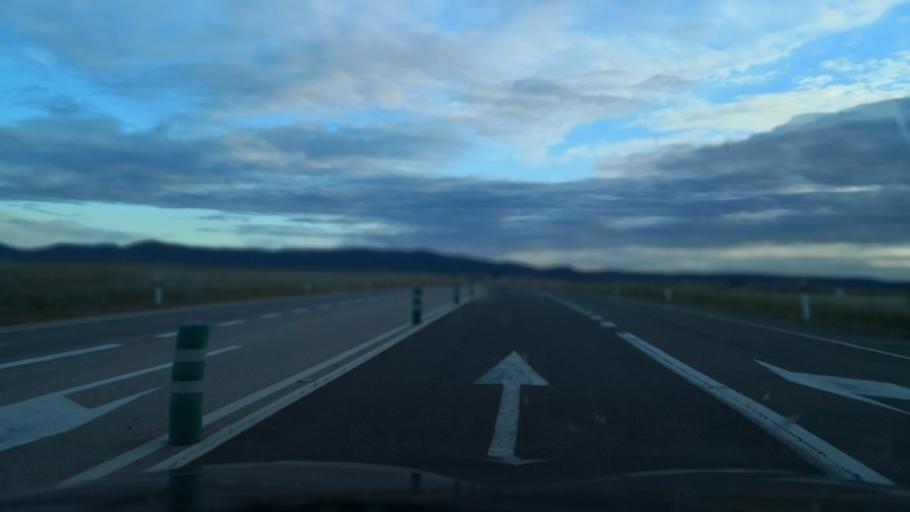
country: ES
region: Extremadura
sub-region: Provincia de Caceres
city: Malpartida de Caceres
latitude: 39.3623
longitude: -6.4625
